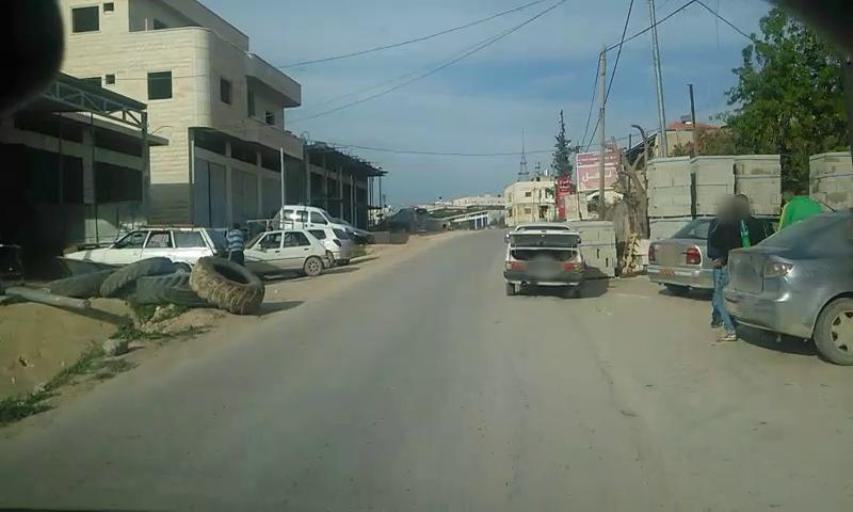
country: PS
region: West Bank
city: Bayt Ula
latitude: 31.6047
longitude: 35.0143
